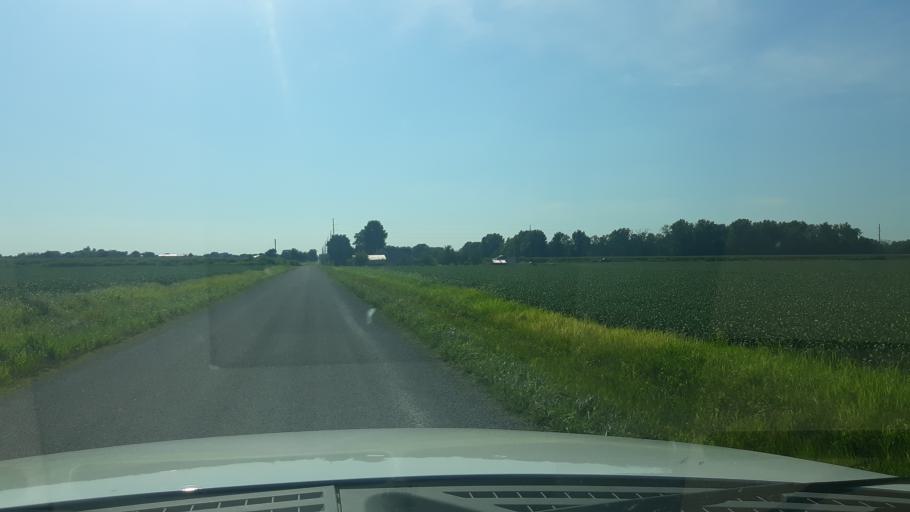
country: US
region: Illinois
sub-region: Saline County
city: Eldorado
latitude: 37.8630
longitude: -88.5008
